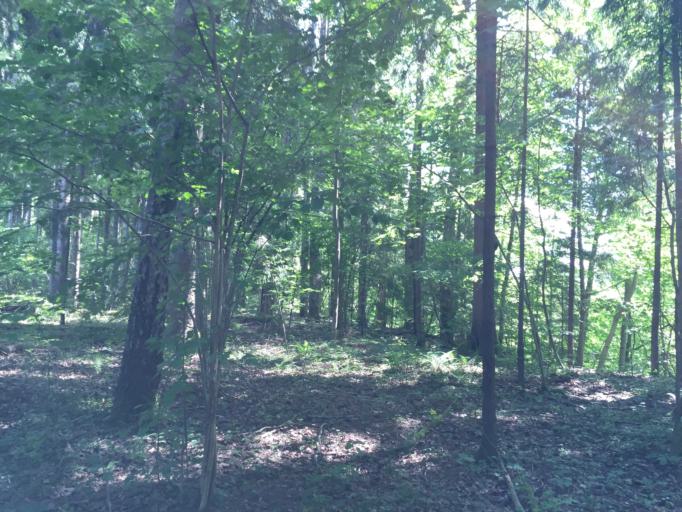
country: LV
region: Sigulda
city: Sigulda
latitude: 57.1902
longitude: 24.9304
